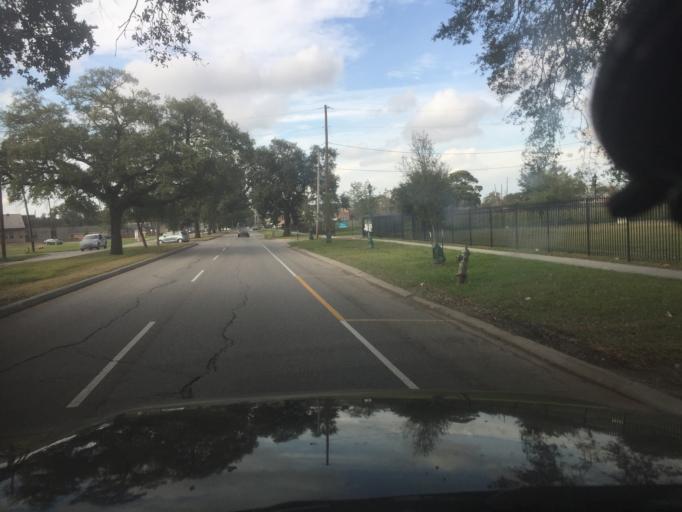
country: US
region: Louisiana
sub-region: Orleans Parish
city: New Orleans
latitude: 29.9971
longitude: -90.0796
